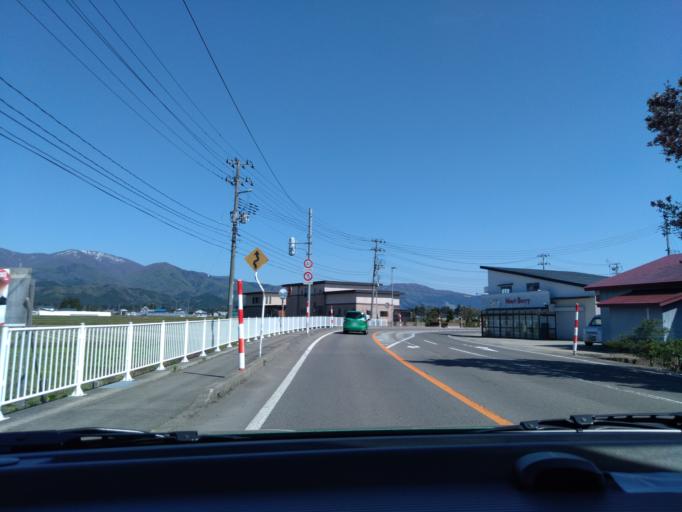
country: JP
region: Akita
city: Kakunodatemachi
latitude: 39.5714
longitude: 140.5800
